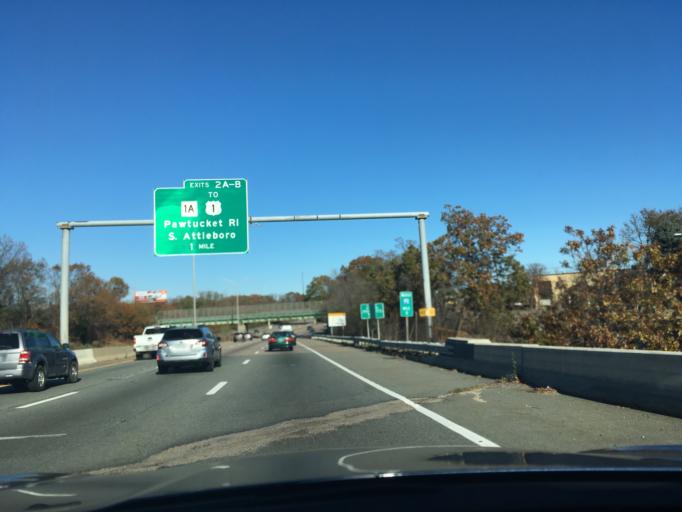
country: US
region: Rhode Island
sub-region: Providence County
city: Central Falls
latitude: 41.8943
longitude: -71.3759
